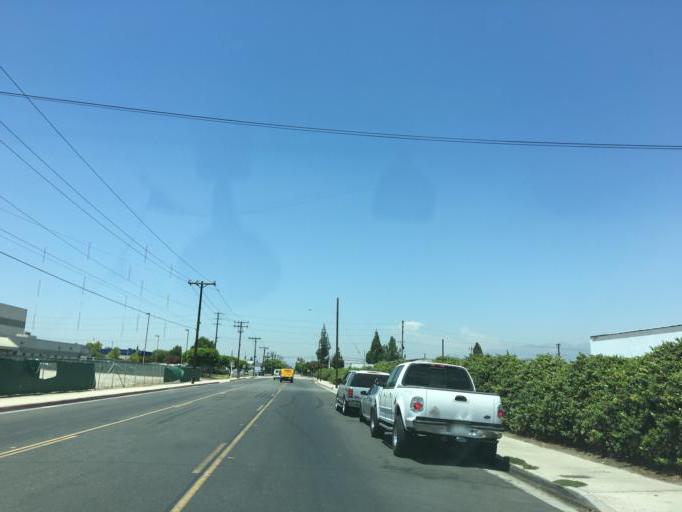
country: US
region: California
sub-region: Los Angeles County
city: Avocado Heights
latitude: 34.0307
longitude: -117.9757
